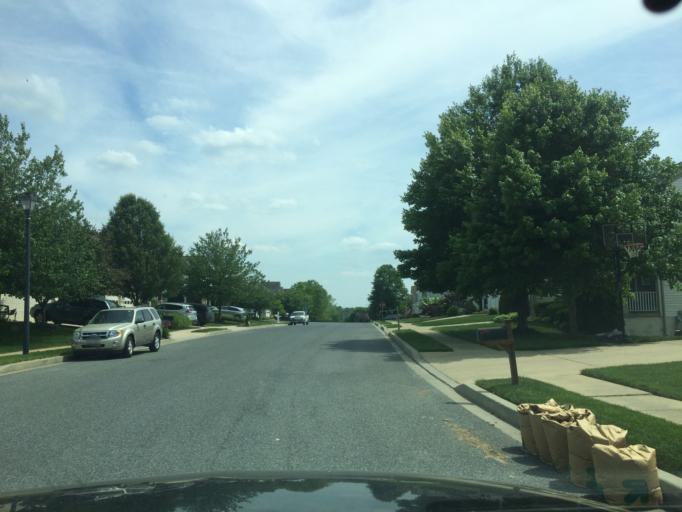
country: US
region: Maryland
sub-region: Carroll County
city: Sykesville
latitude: 39.3791
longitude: -76.9786
